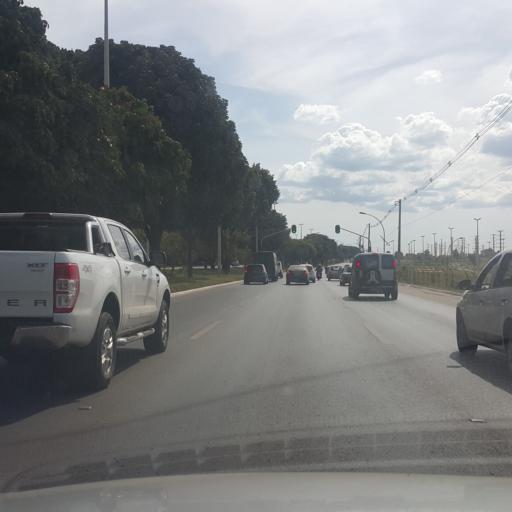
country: BR
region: Federal District
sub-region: Brasilia
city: Brasilia
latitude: -15.8060
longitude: -48.0579
